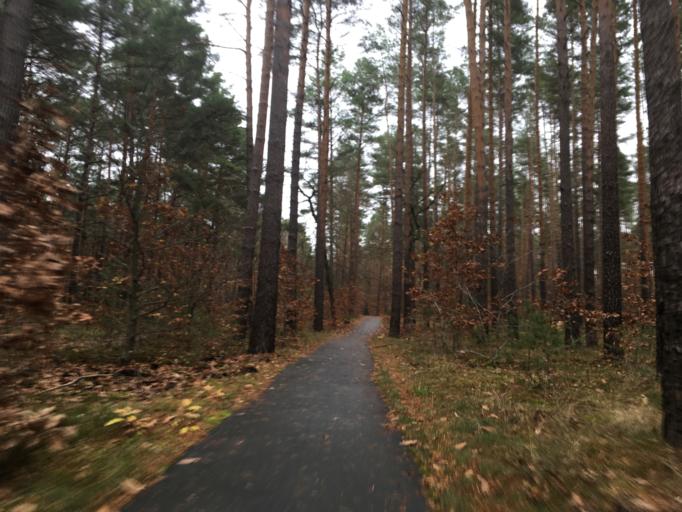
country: DE
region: Brandenburg
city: Mixdorf
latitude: 52.1507
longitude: 14.4282
